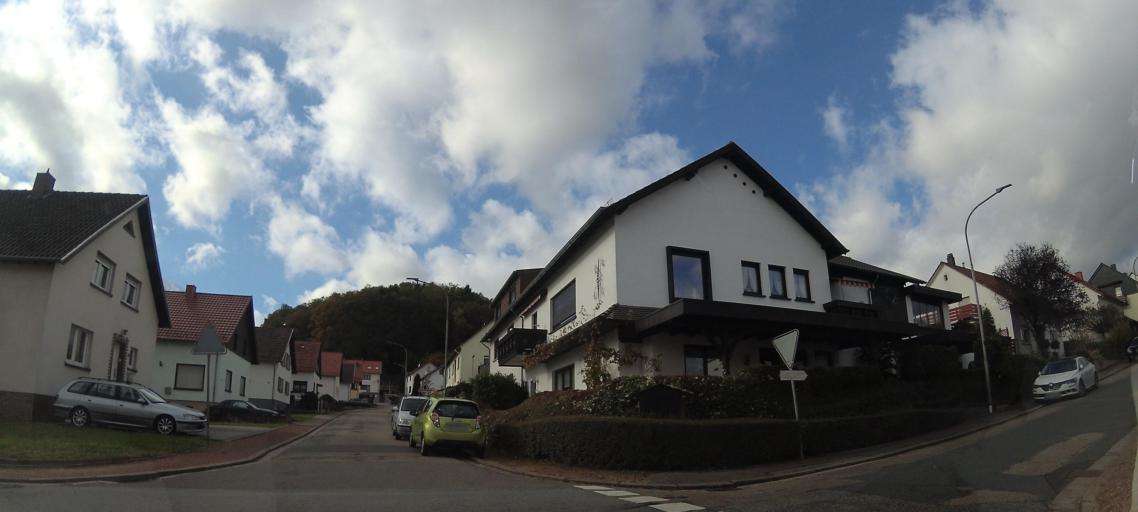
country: DE
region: Saarland
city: Blieskastel
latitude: 49.2549
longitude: 7.2489
